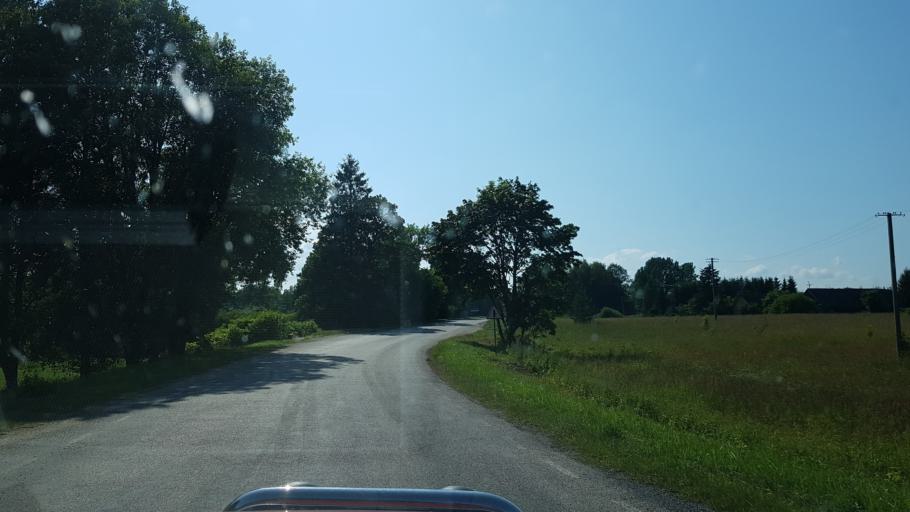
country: EE
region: Tartu
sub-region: Alatskivi vald
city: Kallaste
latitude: 58.6737
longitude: 27.0348
